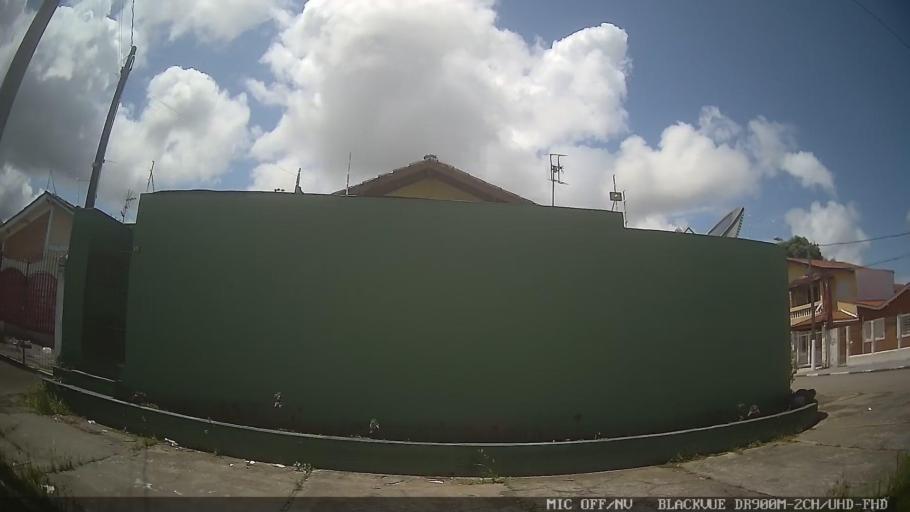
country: BR
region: Sao Paulo
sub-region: Caraguatatuba
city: Caraguatatuba
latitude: -23.6301
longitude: -45.4236
